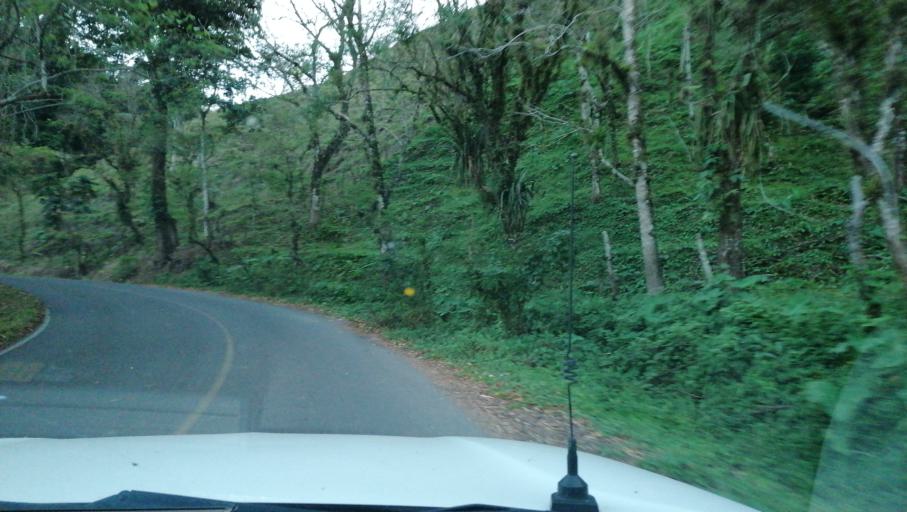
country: MX
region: Chiapas
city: Ostuacan
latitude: 17.4253
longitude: -93.3416
